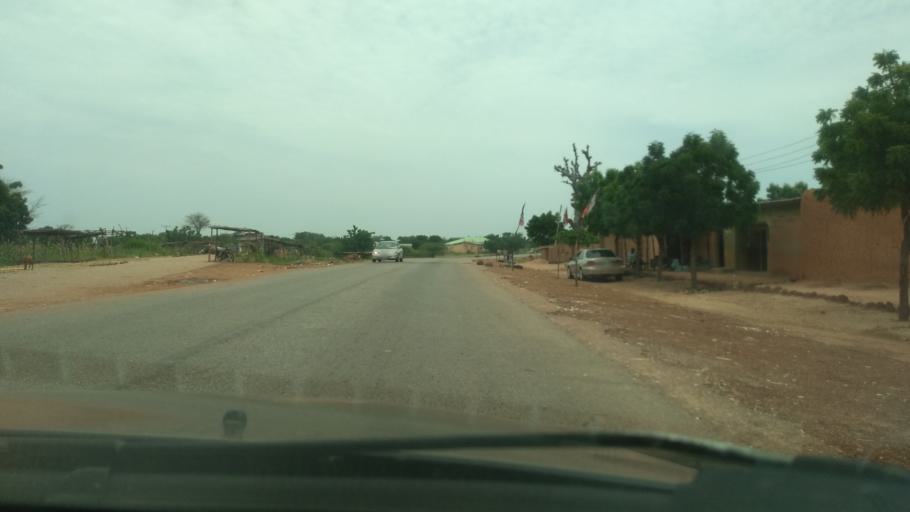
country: NG
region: Katsina
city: Kankia
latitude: 12.4054
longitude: 7.7199
